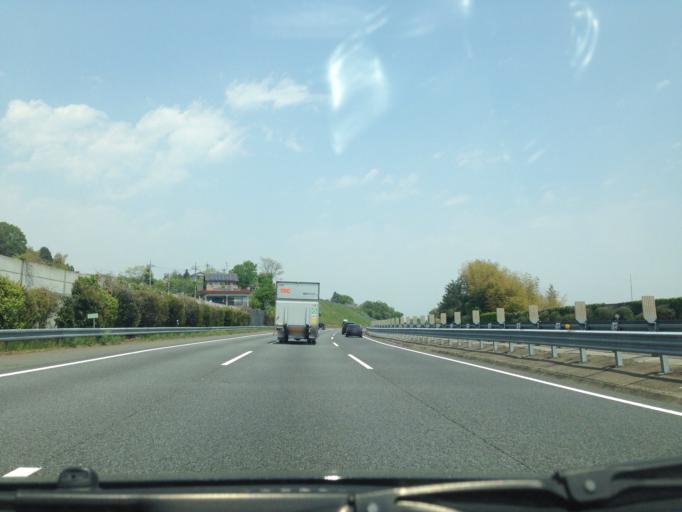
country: JP
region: Tochigi
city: Kanuma
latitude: 36.4759
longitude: 139.7284
